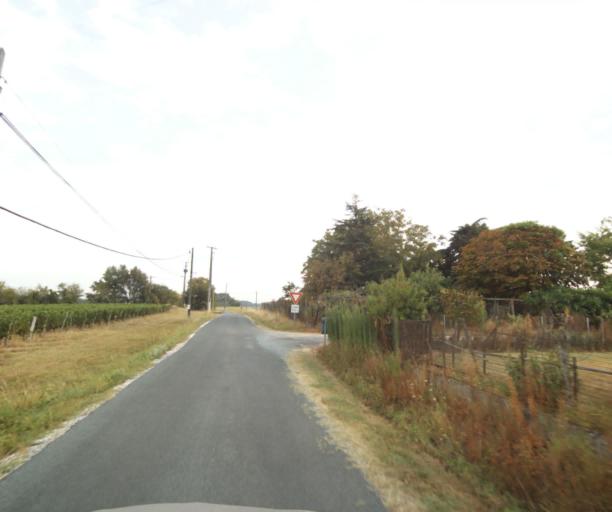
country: FR
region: Aquitaine
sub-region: Departement de la Gironde
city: Creon
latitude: 44.7778
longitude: -0.3395
